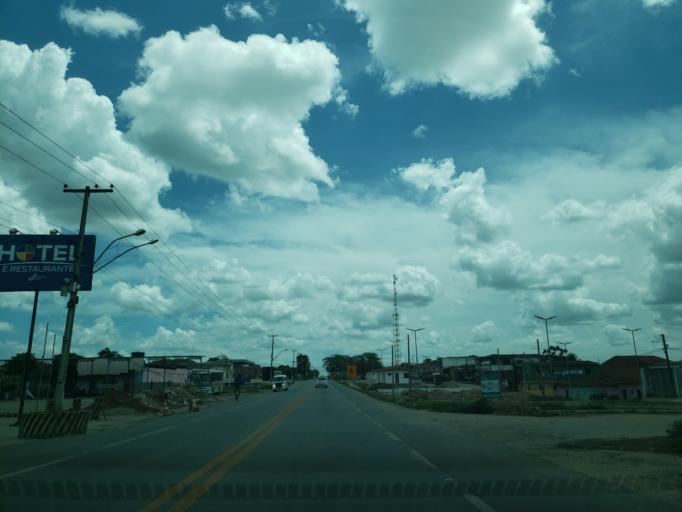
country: BR
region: Alagoas
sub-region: Uniao Dos Palmares
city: Uniao dos Palmares
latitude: -9.1629
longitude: -36.0180
